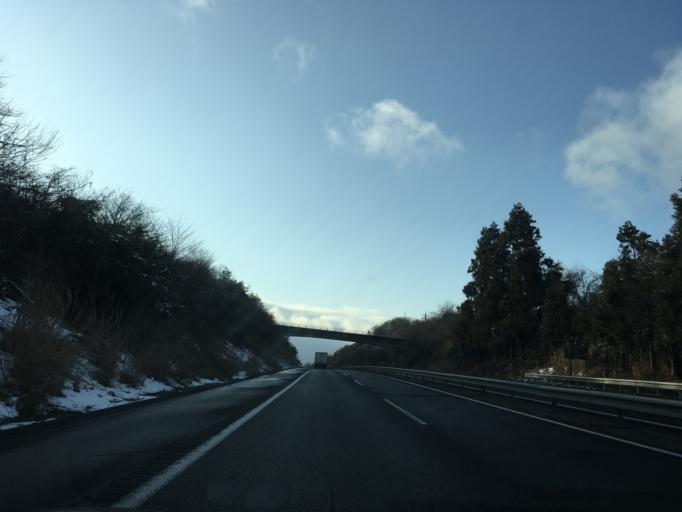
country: JP
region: Miyagi
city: Okawara
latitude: 38.1597
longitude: 140.6710
